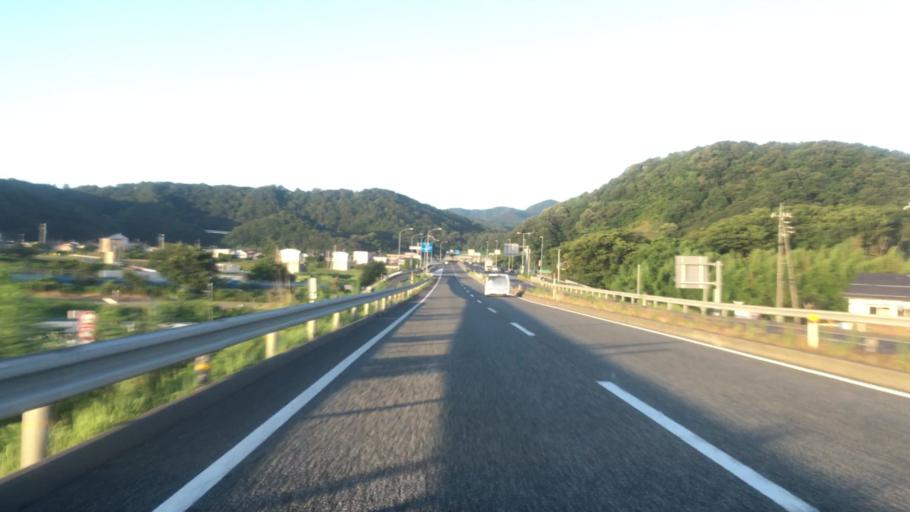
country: JP
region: Tottori
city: Tottori
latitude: 35.5222
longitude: 134.2169
